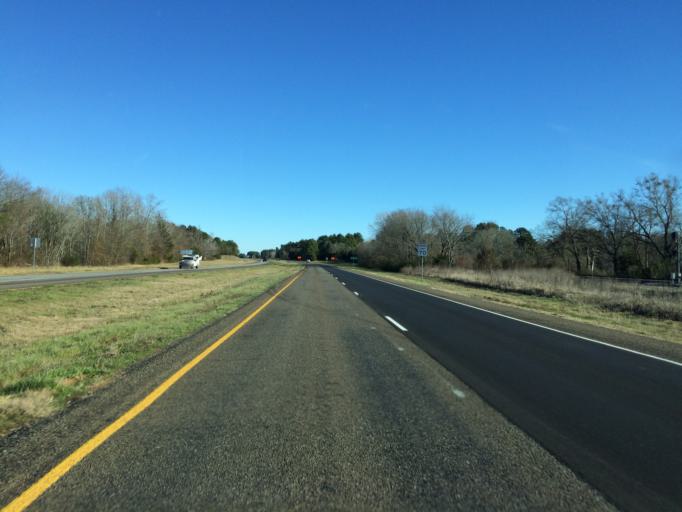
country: US
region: Texas
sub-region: Wood County
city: Hawkins
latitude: 32.6029
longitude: -95.2755
